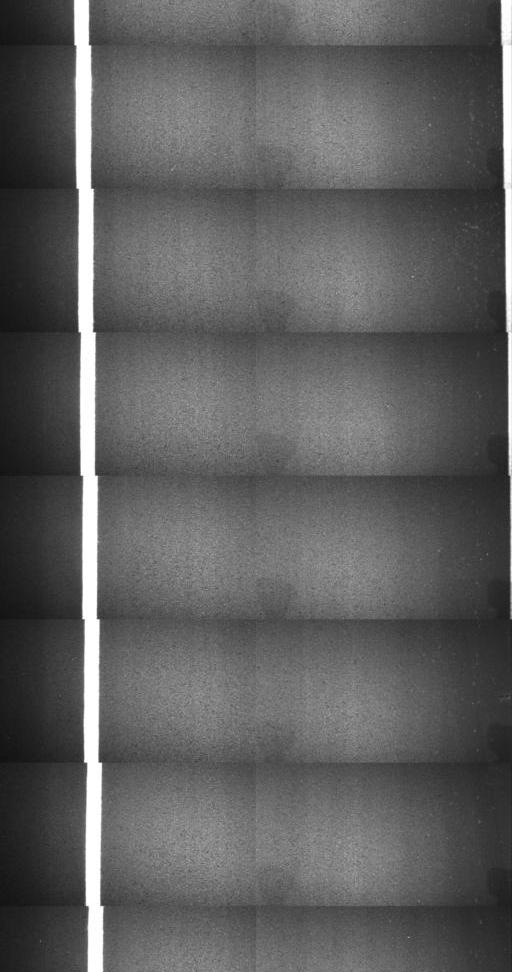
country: US
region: Vermont
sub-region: Caledonia County
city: Lyndonville
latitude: 44.6211
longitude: -71.9064
